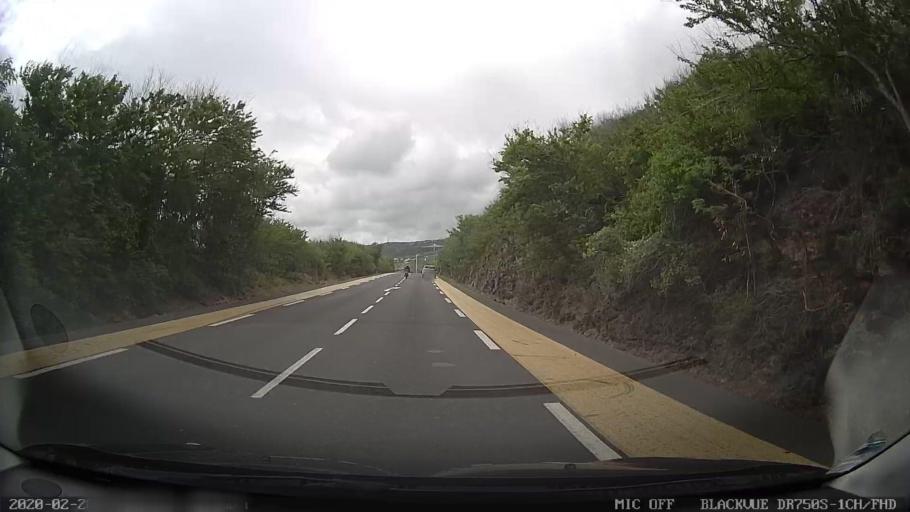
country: RE
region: Reunion
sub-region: Reunion
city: Saint-Leu
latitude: -21.1346
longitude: 55.2719
